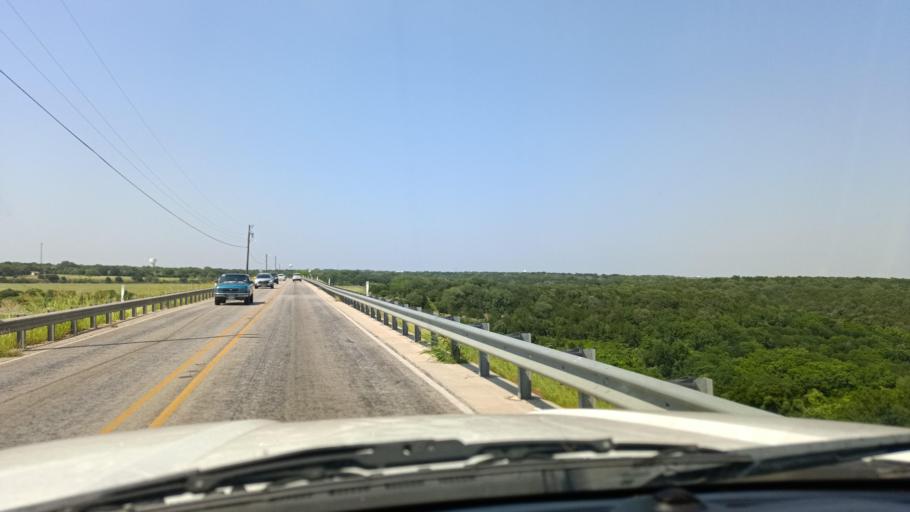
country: US
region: Texas
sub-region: Bell County
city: Morgans Point Resort
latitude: 31.1079
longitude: -97.4729
